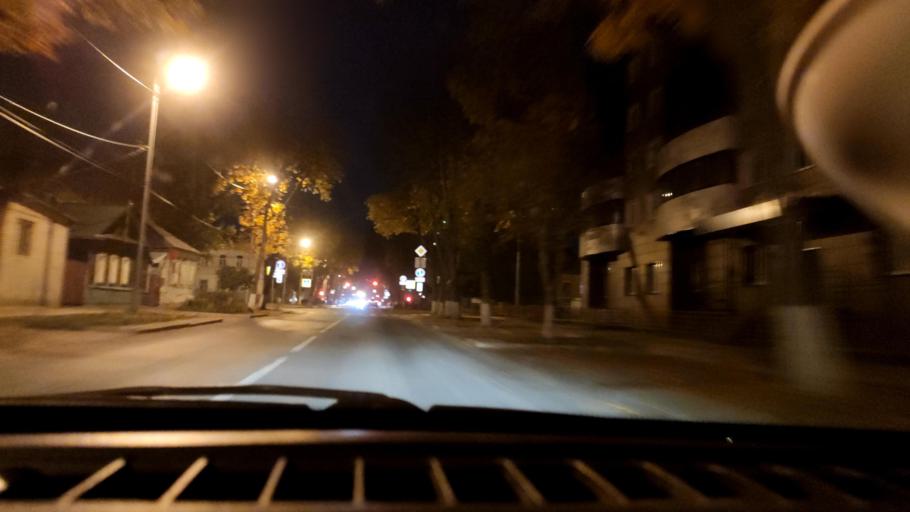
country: RU
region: Samara
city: Samara
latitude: 53.1997
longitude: 50.1196
